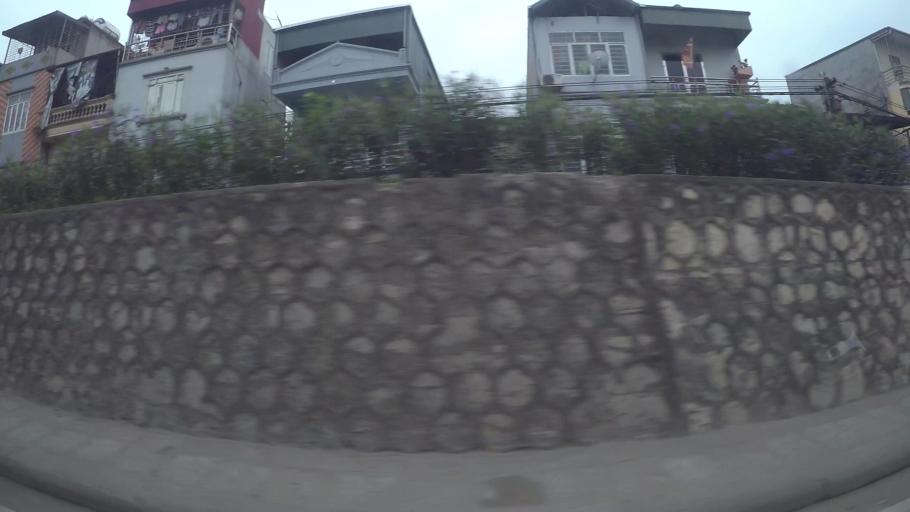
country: VN
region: Ha Noi
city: Hai BaTrung
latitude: 21.0008
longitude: 105.8843
